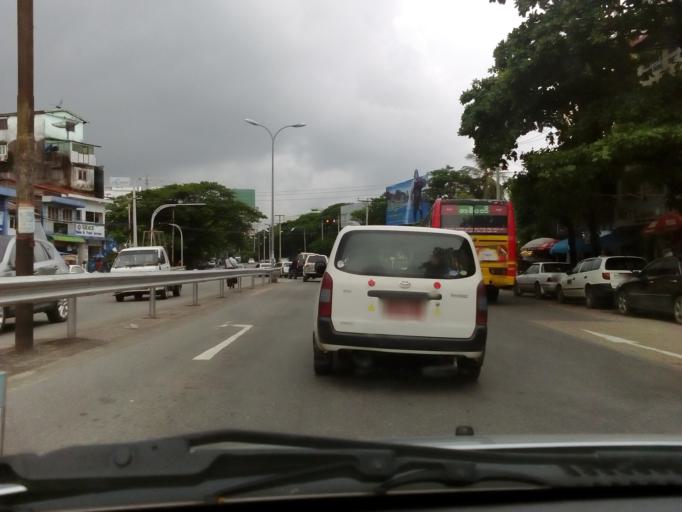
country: MM
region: Yangon
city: Yangon
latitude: 16.8225
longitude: 96.1627
